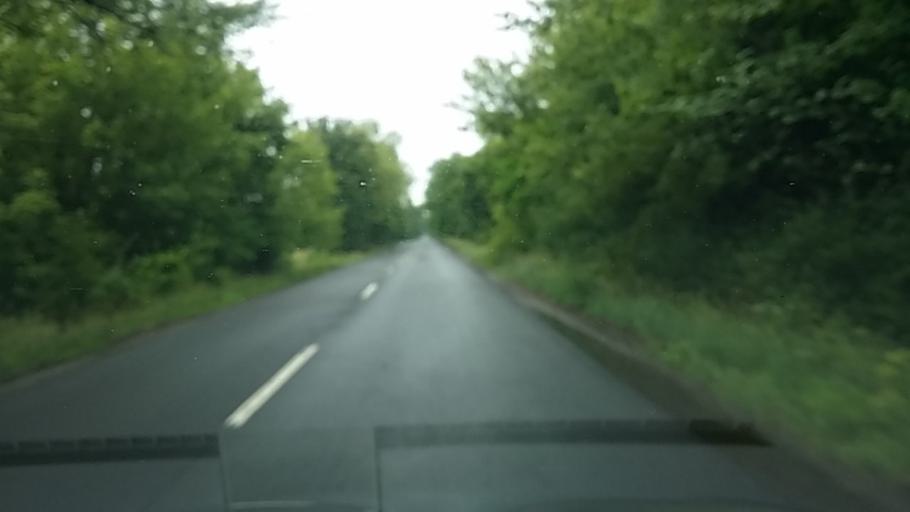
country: SK
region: Nitriansky
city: Zeliezovce
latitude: 47.9627
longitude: 18.7822
